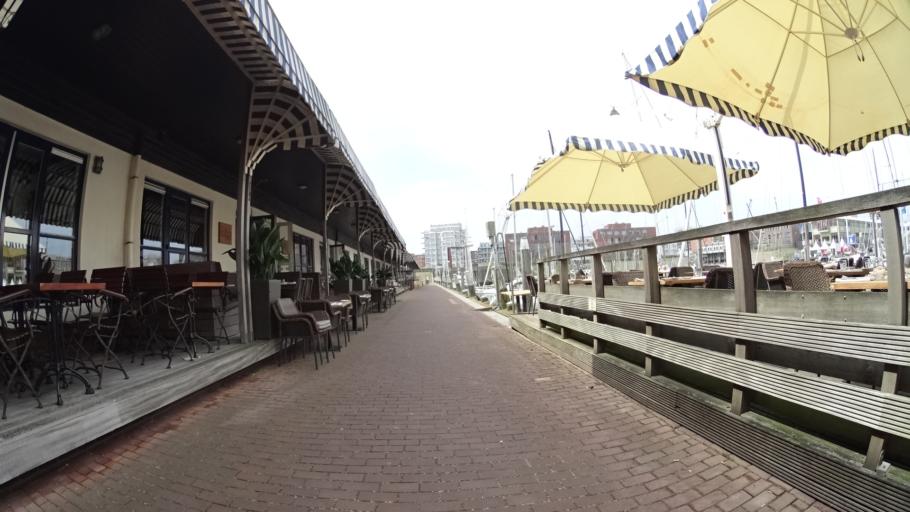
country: NL
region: South Holland
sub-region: Gemeente Den Haag
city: Scheveningen
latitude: 52.0952
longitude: 4.2656
